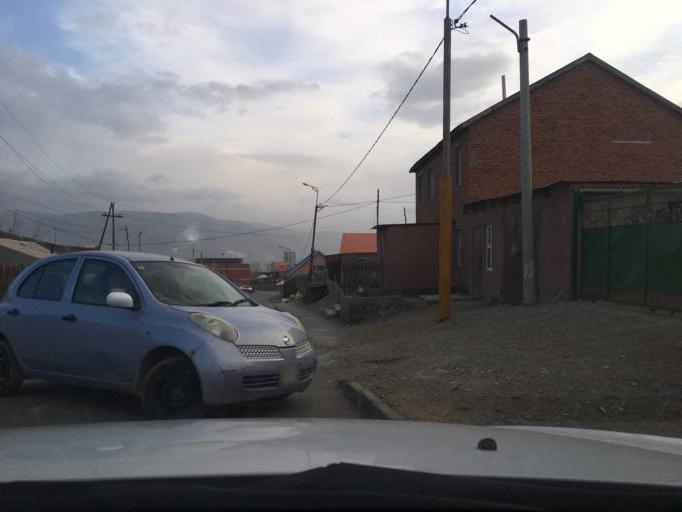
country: MN
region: Ulaanbaatar
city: Ulaanbaatar
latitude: 47.9319
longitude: 106.8582
